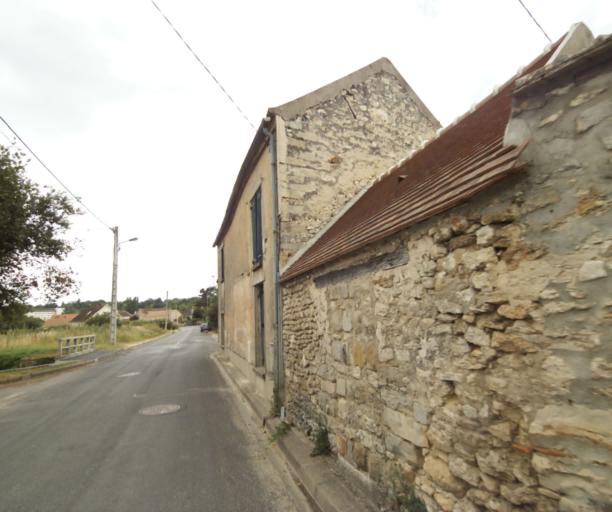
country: FR
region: Ile-de-France
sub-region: Departement de l'Essonne
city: Soisy-sur-Ecole
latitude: 48.4739
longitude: 2.5119
